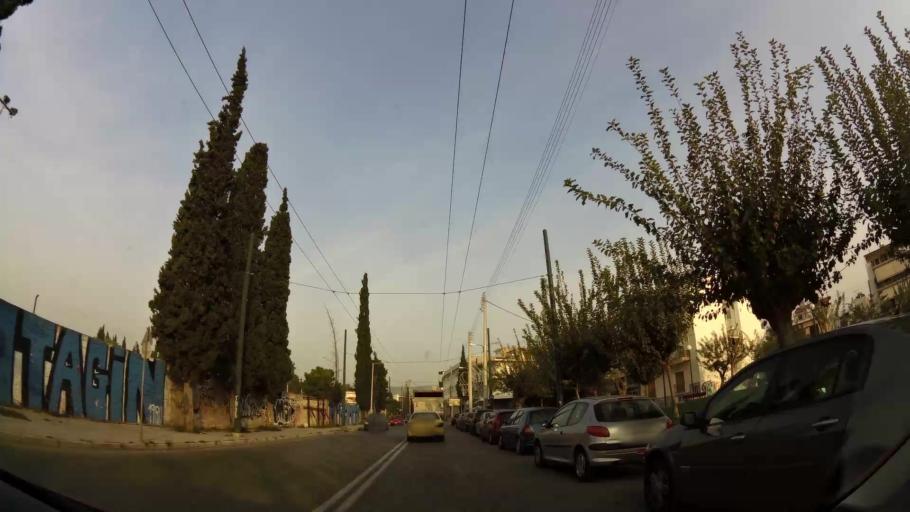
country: GR
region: Attica
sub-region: Nomarchia Athinas
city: Peristeri
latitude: 38.0196
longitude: 23.6879
